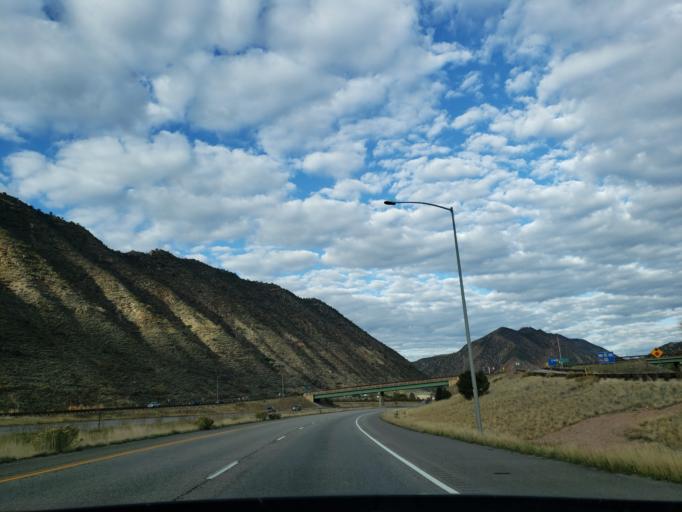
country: US
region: Colorado
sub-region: Garfield County
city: New Castle
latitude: 39.5657
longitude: -107.5139
